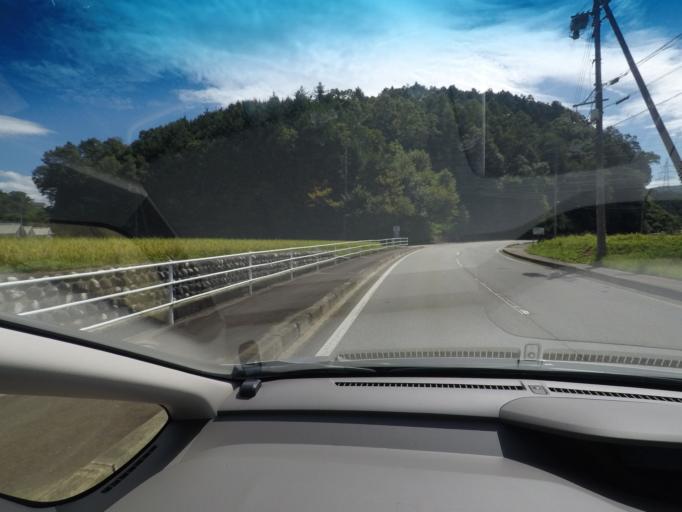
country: JP
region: Gifu
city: Takayama
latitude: 36.1418
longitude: 137.2847
